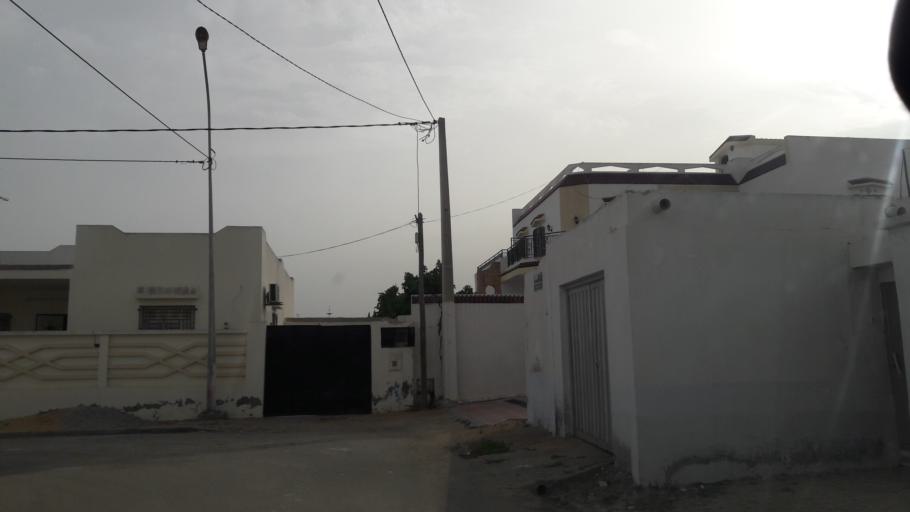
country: TN
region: Safaqis
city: Al Qarmadah
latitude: 34.7760
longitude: 10.7653
